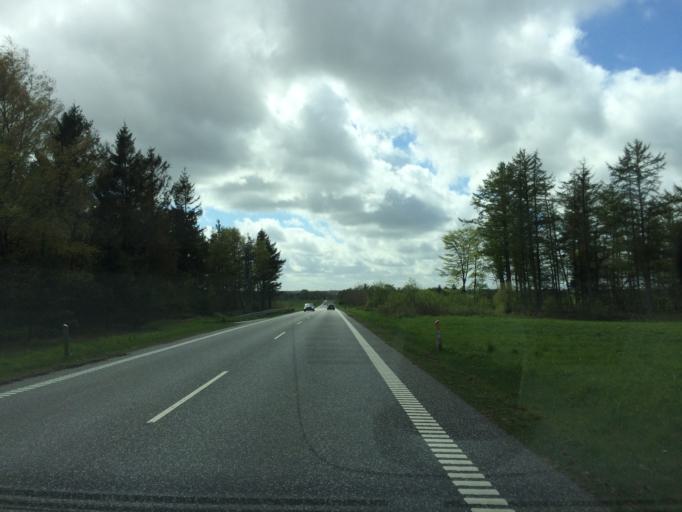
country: DK
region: Central Jutland
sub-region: Viborg Kommune
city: Stoholm
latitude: 56.4134
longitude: 9.0240
